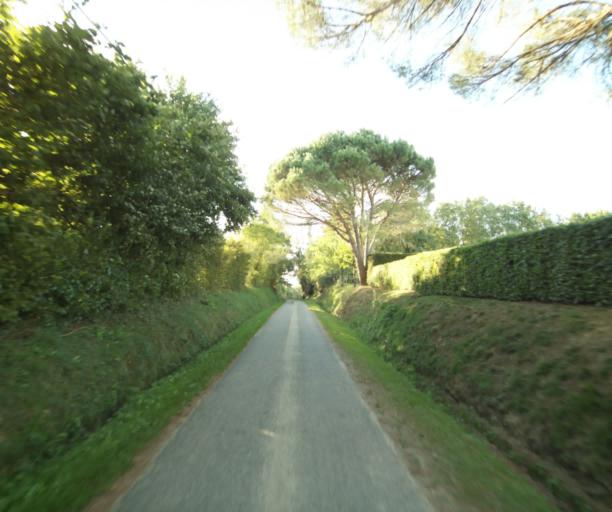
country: FR
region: Midi-Pyrenees
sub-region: Departement du Gers
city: Cazaubon
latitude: 43.8709
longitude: -0.0027
